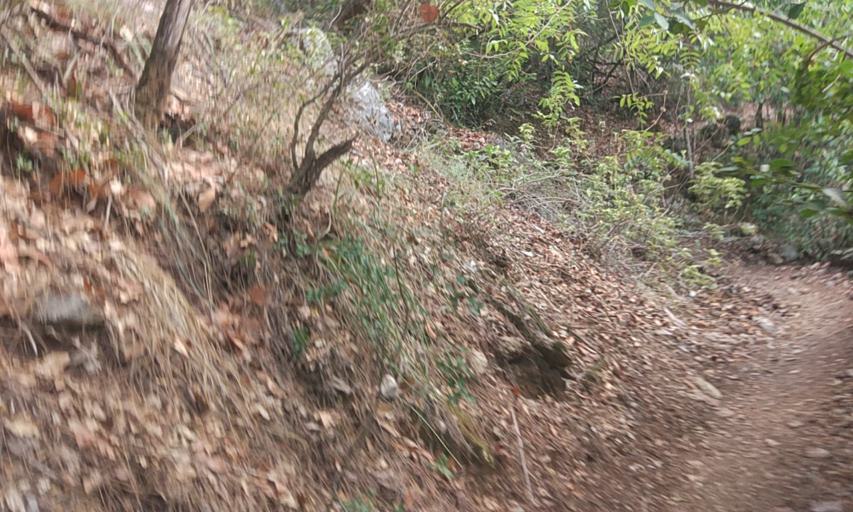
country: TR
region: Antalya
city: Tekirova
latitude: 36.3816
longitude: 30.4757
